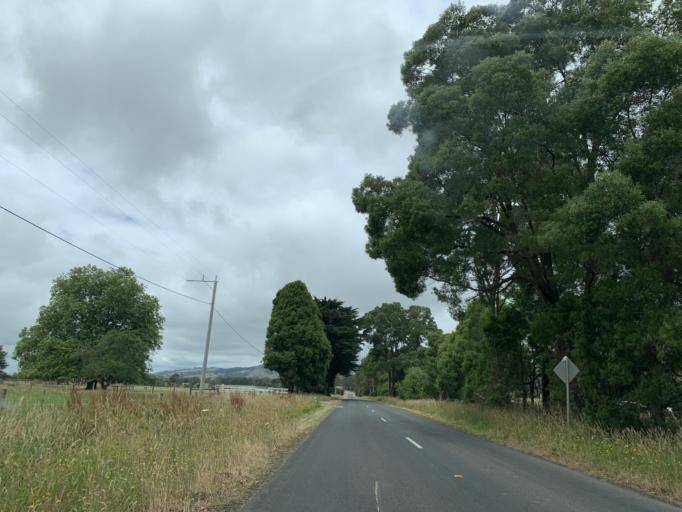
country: AU
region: Victoria
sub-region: Baw Baw
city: Warragul
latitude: -38.2437
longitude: 145.9664
